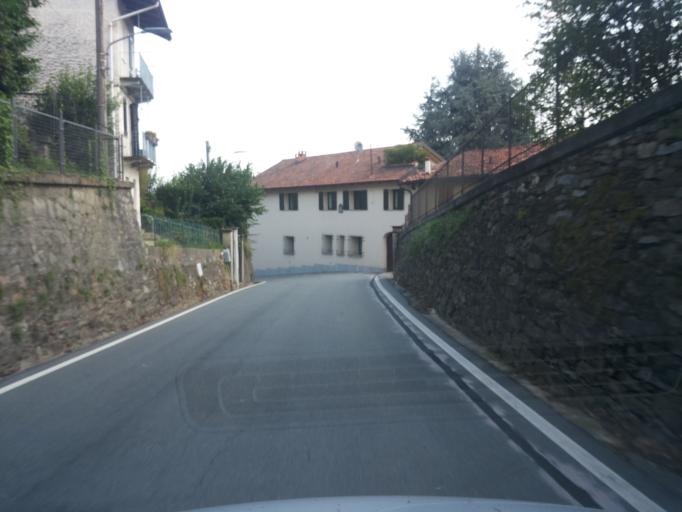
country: IT
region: Piedmont
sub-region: Provincia di Biella
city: Pralungo
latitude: 45.5761
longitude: 8.0428
